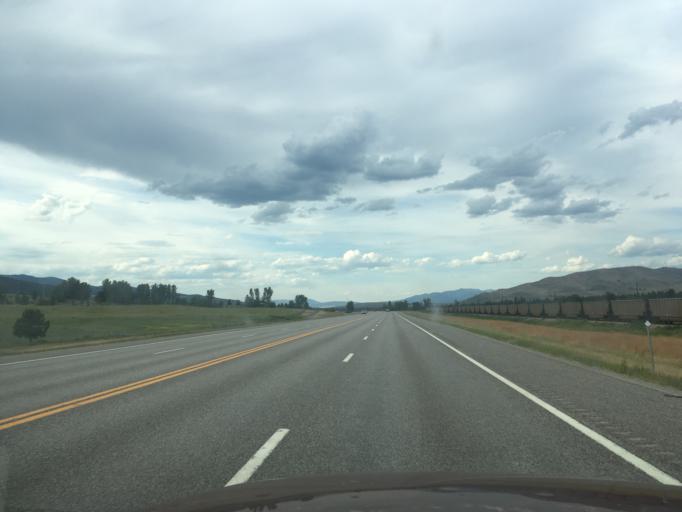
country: US
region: Montana
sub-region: Missoula County
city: Lolo
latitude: 46.6920
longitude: -114.0740
